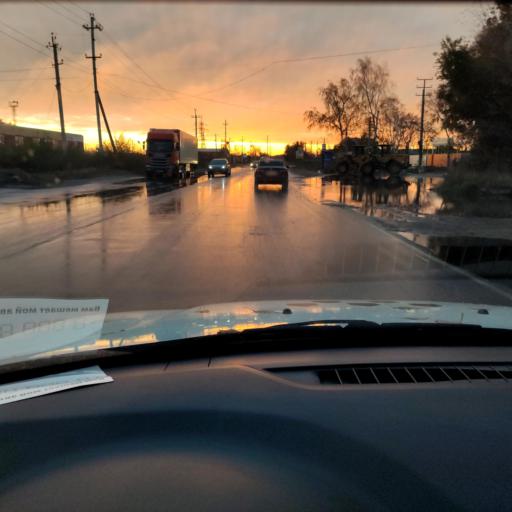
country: RU
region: Samara
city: Tol'yatti
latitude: 53.5290
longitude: 49.4706
